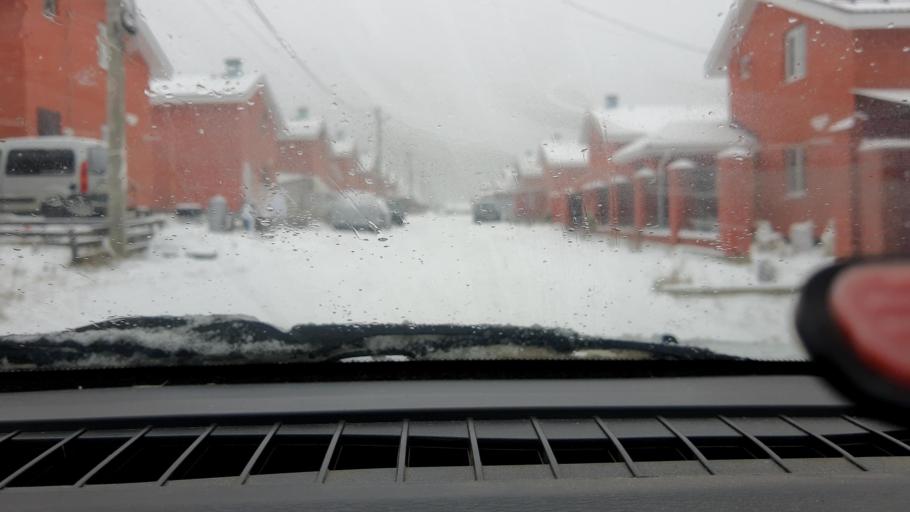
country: RU
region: Nizjnij Novgorod
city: Afonino
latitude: 56.1945
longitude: 44.0878
